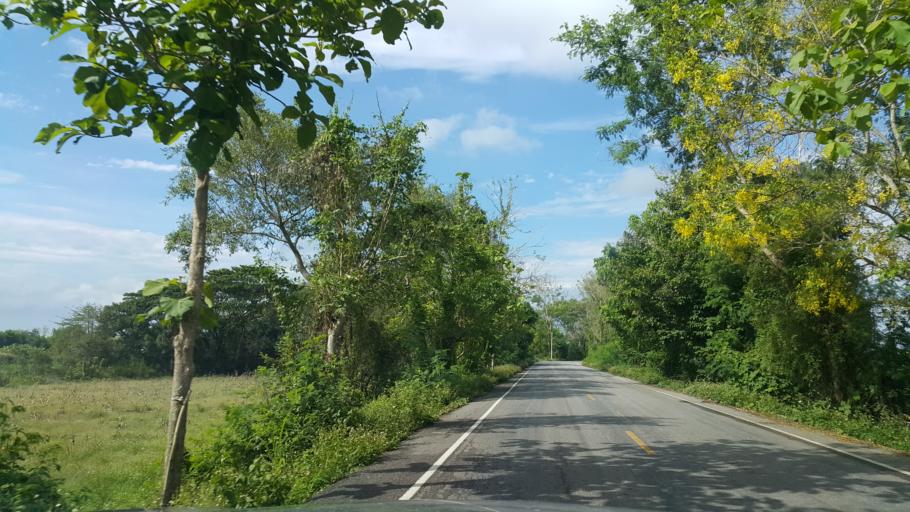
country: TH
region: Chiang Rai
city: Wiang Chai
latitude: 19.9317
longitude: 99.9080
